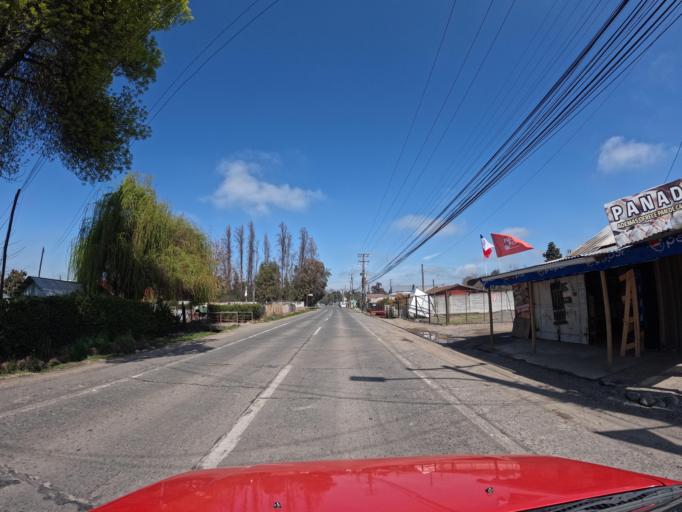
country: CL
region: Maule
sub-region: Provincia de Curico
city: Molina
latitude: -35.0820
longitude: -71.2632
